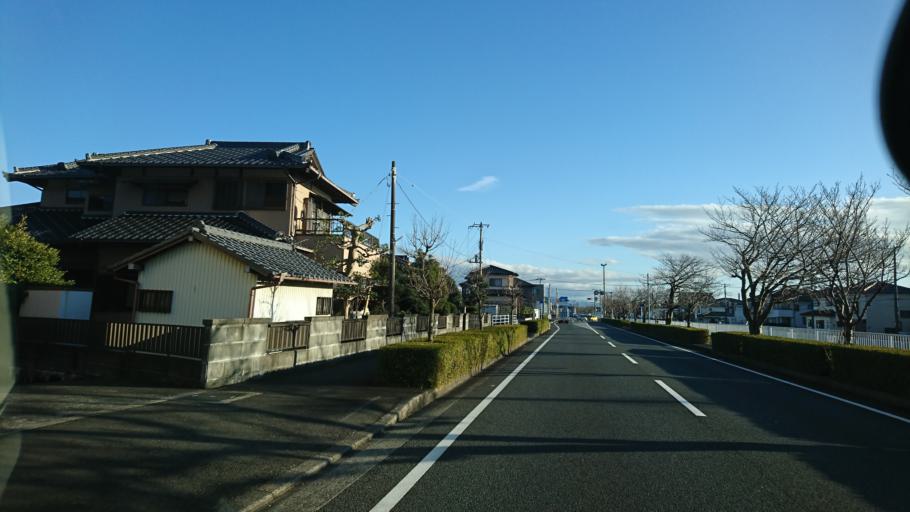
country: JP
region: Shizuoka
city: Fuji
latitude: 35.1376
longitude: 138.6517
